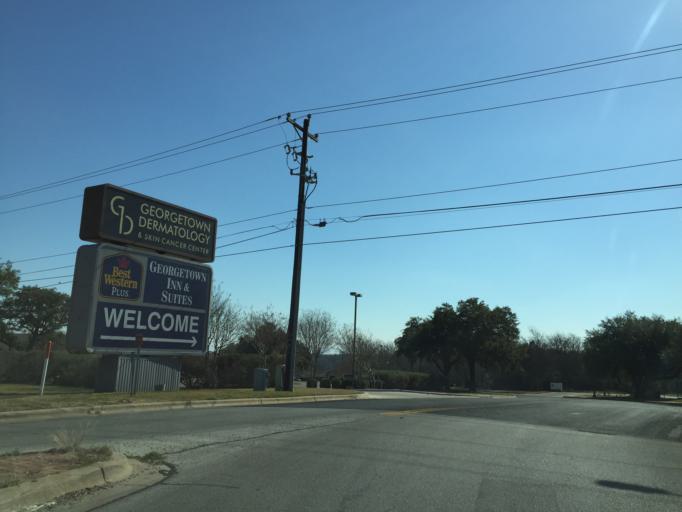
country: US
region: Texas
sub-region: Williamson County
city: Georgetown
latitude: 30.6441
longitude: -97.6846
